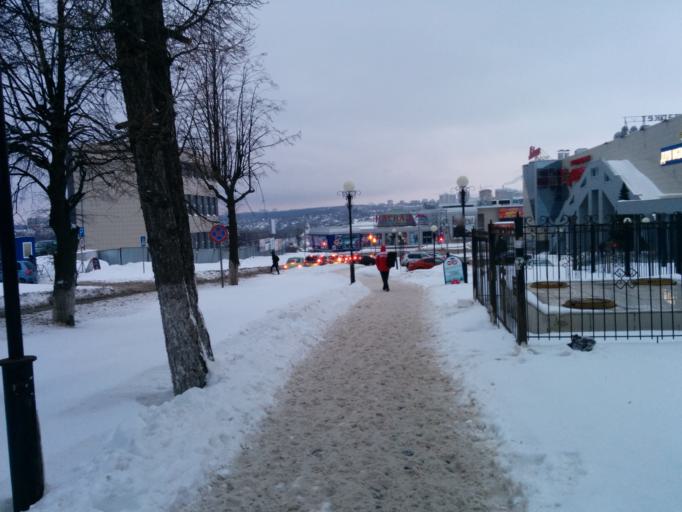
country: RU
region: Chuvashia
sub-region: Cheboksarskiy Rayon
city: Cheboksary
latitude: 56.1346
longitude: 47.2438
